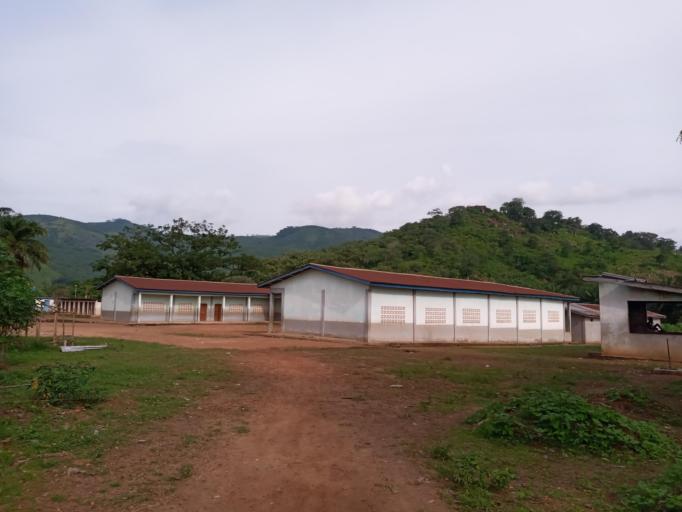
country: SL
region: Northern Province
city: Bumbuna
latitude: 9.0460
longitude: -11.7527
